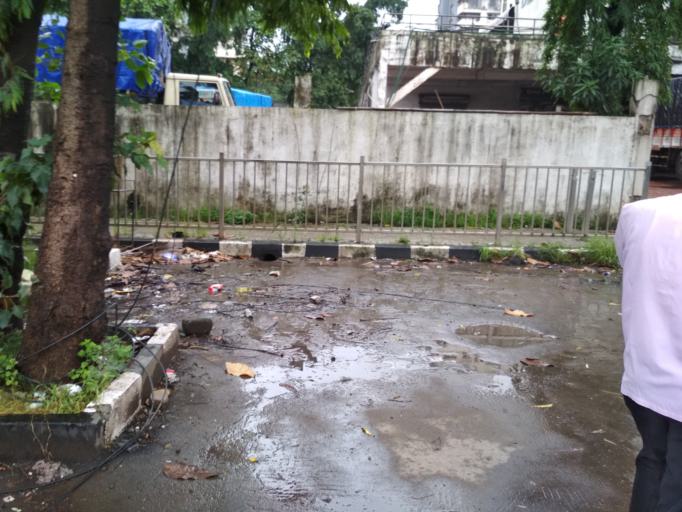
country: IN
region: Maharashtra
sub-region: Thane
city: Thane
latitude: 19.1636
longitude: 72.9397
